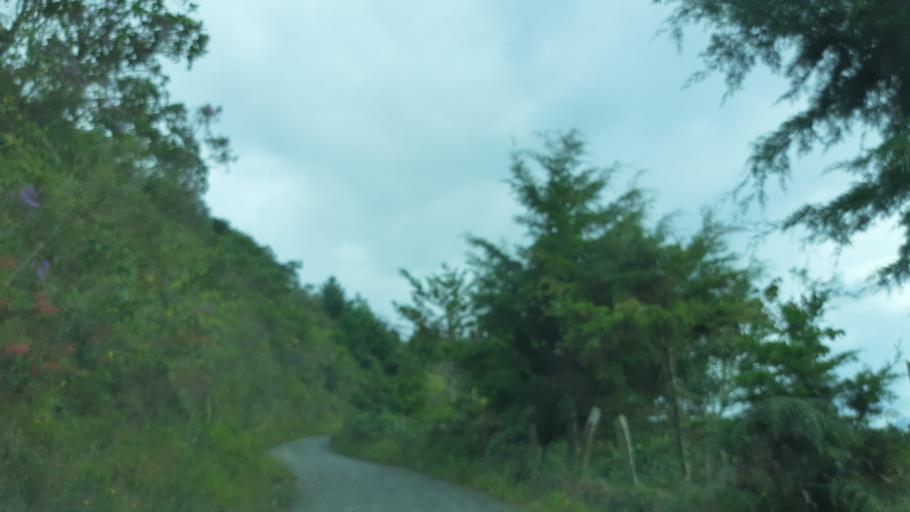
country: CO
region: Boyaca
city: Garagoa
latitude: 5.0025
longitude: -73.3382
